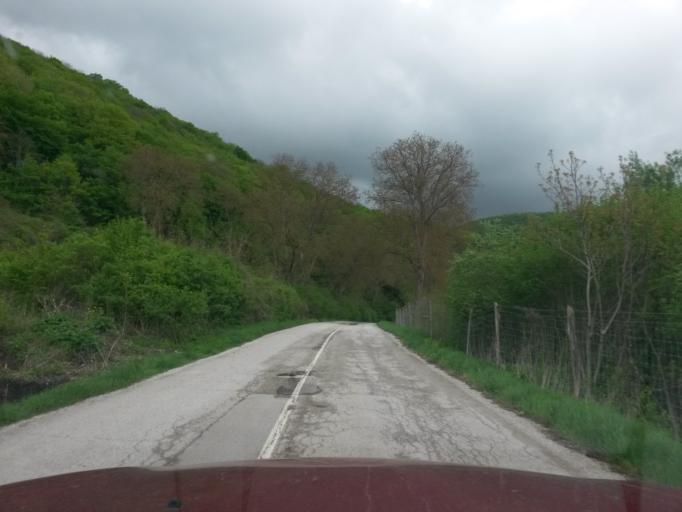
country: SK
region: Kosicky
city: Roznava
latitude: 48.5690
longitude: 20.4663
